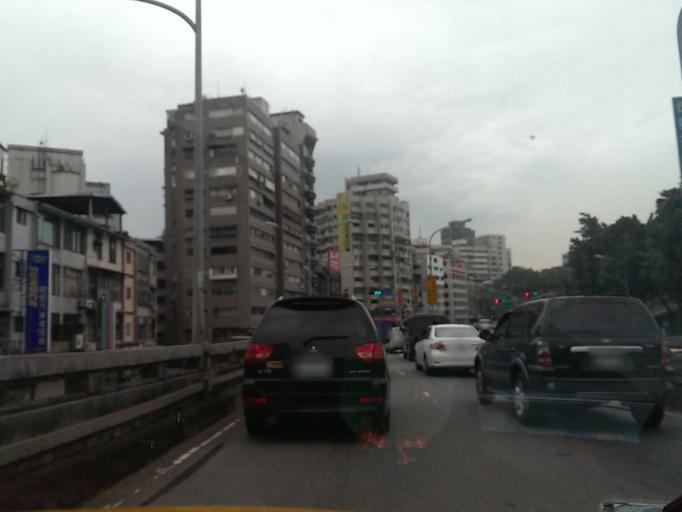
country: TW
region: Taipei
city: Taipei
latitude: 25.0208
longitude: 121.5240
